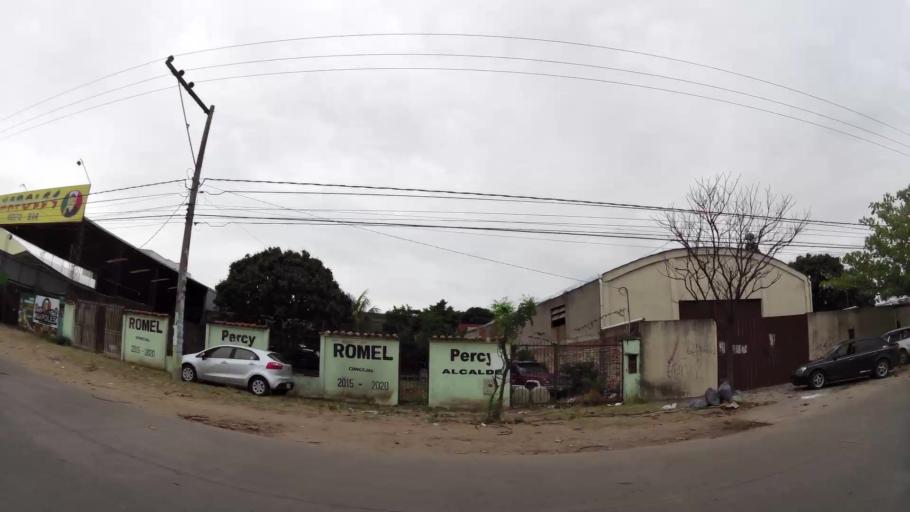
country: BO
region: Santa Cruz
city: Santa Cruz de la Sierra
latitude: -17.8085
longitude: -63.1567
